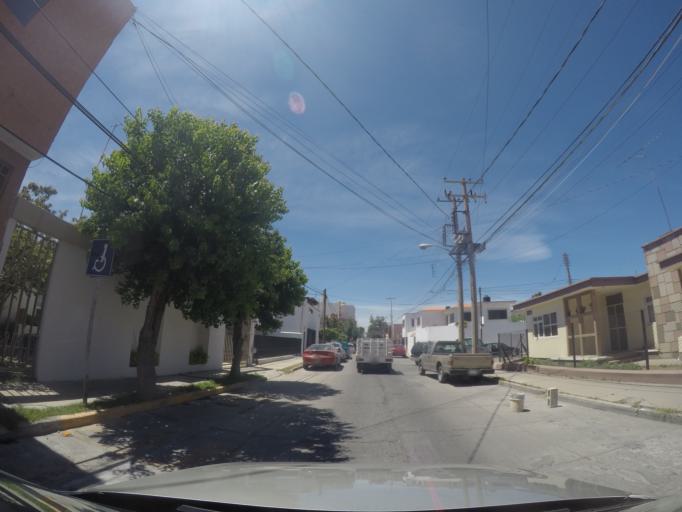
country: MX
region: San Luis Potosi
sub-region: San Luis Potosi
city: San Luis Potosi
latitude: 22.1549
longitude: -100.9948
